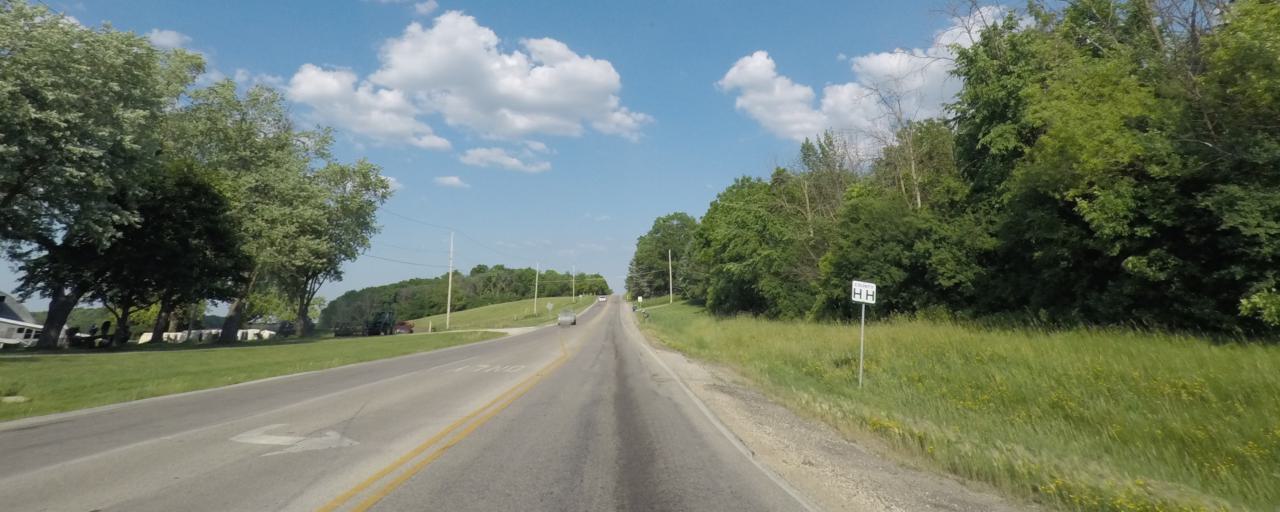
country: US
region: Wisconsin
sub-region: Waukesha County
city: Muskego
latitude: 42.9300
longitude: -88.1133
